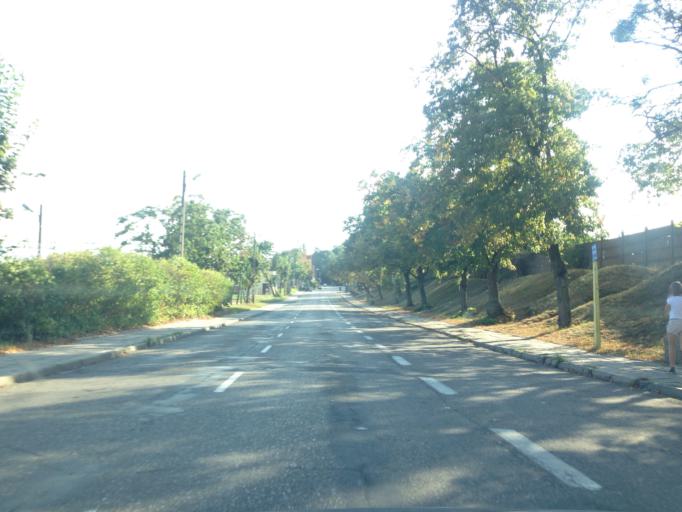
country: PL
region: Warmian-Masurian Voivodeship
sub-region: Powiat ilawski
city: Ilawa
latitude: 53.5853
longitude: 19.5749
